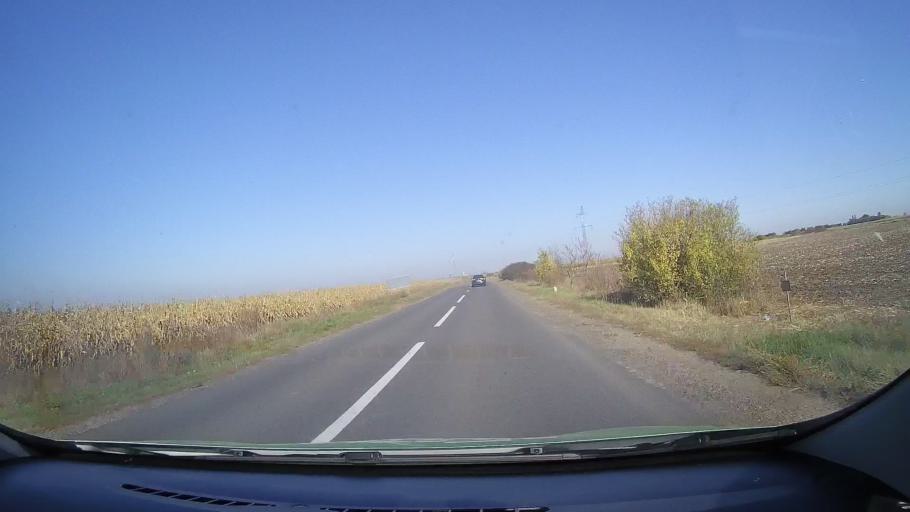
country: RO
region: Satu Mare
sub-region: Comuna Cauas
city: Cauas
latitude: 47.6047
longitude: 22.5427
